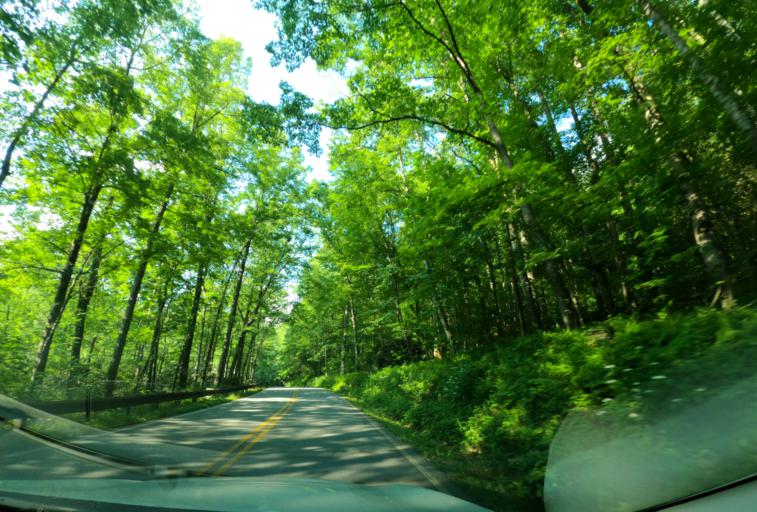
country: US
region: North Carolina
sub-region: Transylvania County
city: Brevard
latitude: 35.1564
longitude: -82.8321
